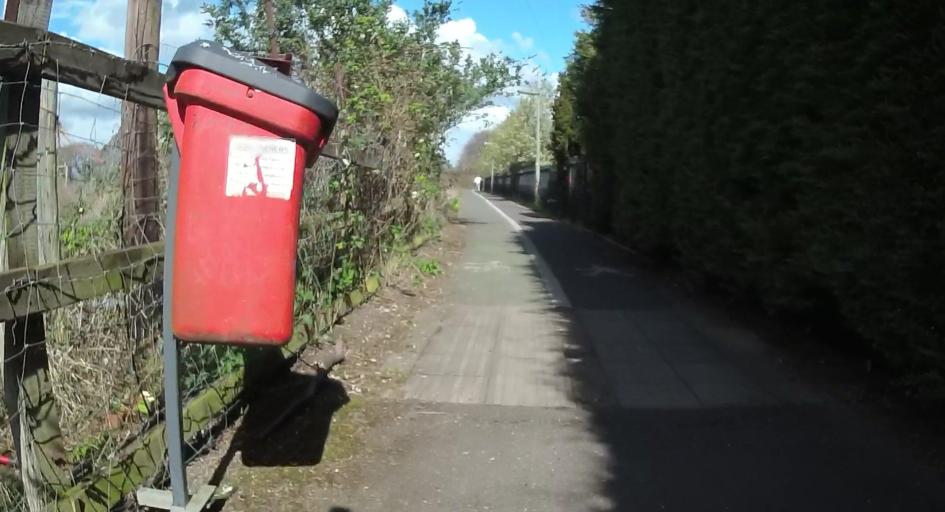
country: GB
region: England
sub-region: Surrey
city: Addlestone
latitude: 51.3764
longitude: -0.5039
